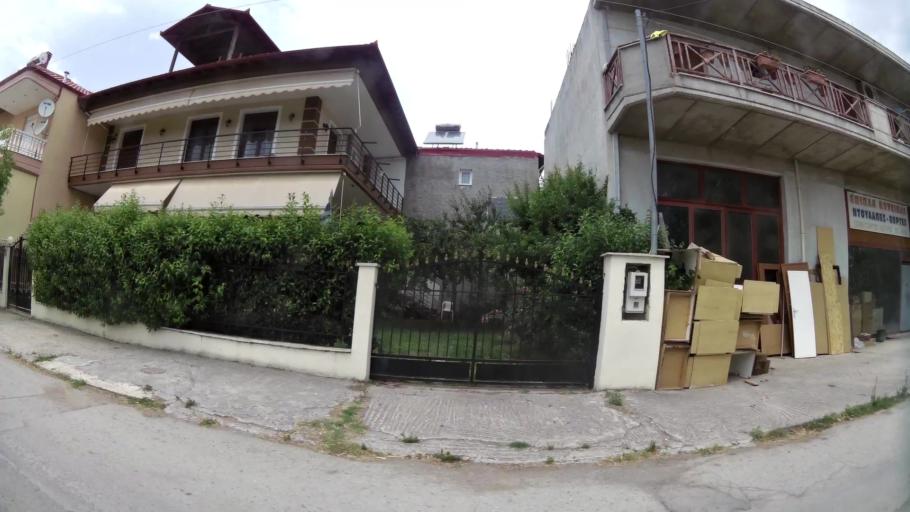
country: GR
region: Central Macedonia
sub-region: Nomos Pierias
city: Kallithea
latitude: 40.2778
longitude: 22.5787
